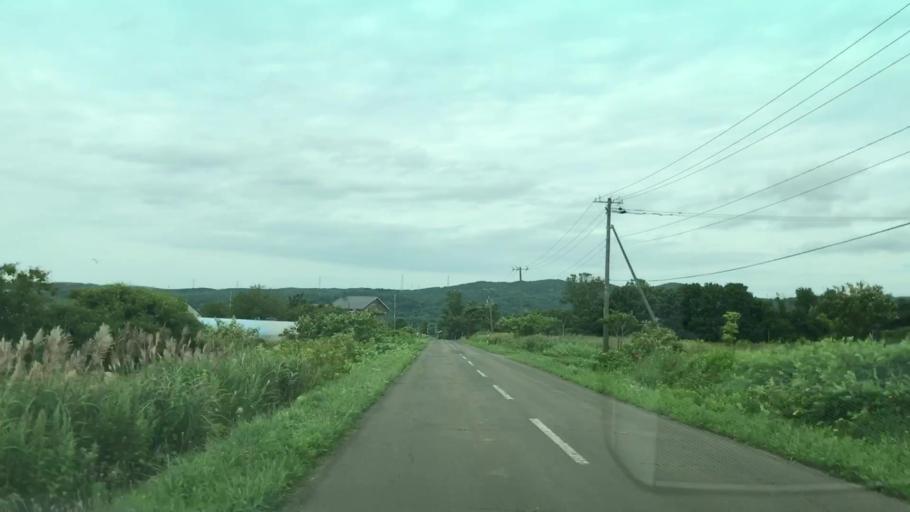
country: JP
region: Hokkaido
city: Iwanai
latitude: 43.0321
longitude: 140.5683
